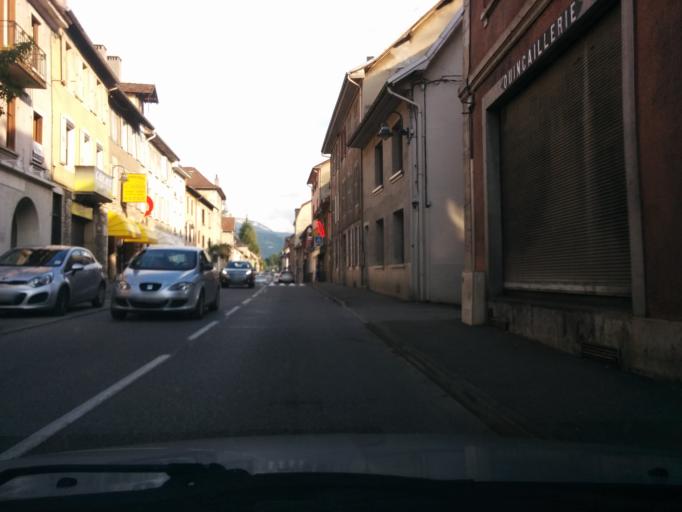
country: FR
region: Rhone-Alpes
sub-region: Departement de la Savoie
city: Le Pont-de-Beauvoisin
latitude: 45.5350
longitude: 5.6746
